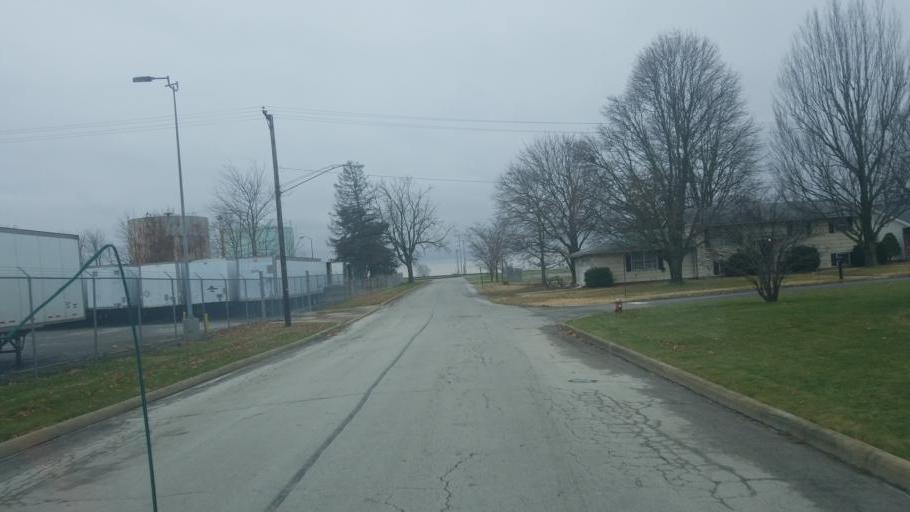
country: US
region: Ohio
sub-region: Crawford County
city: Bucyrus
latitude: 40.7925
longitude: -82.9741
